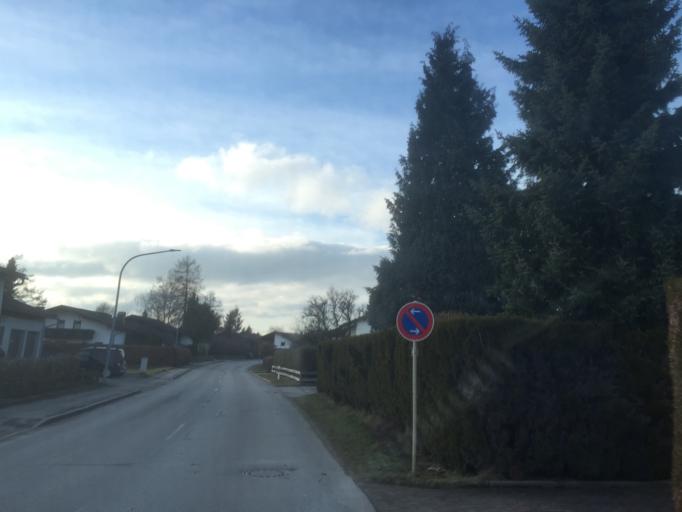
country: DE
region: Bavaria
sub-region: Upper Bavaria
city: Vachendorf
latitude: 47.8440
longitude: 12.6067
